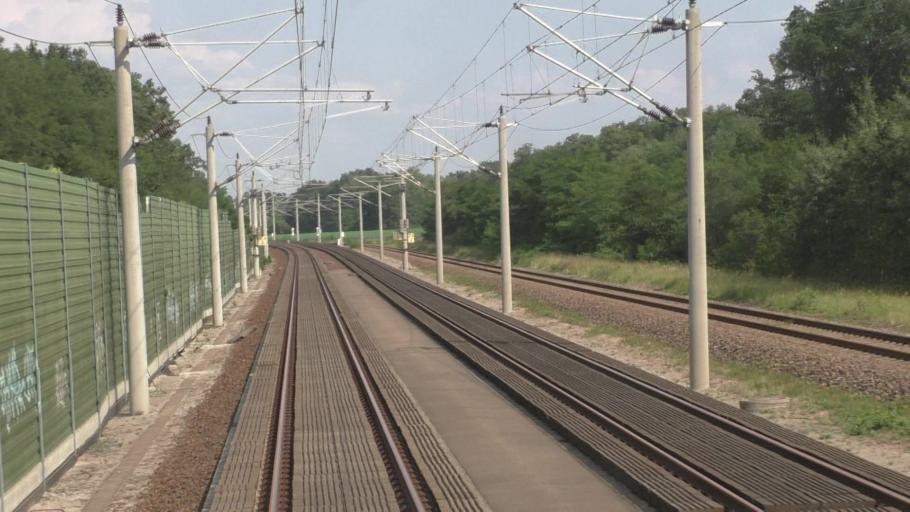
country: DE
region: Brandenburg
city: Rathenow
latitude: 52.5911
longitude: 12.3046
